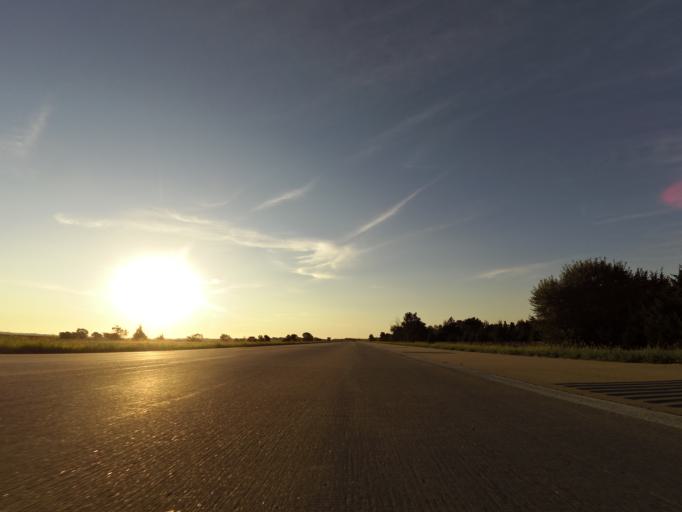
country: US
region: Kansas
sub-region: Reno County
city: Haven
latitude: 37.8811
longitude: -97.7175
